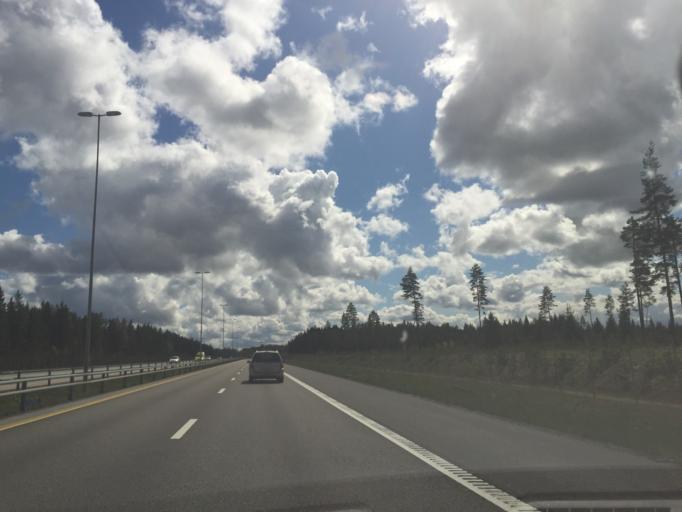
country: NO
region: Akershus
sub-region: Ullensaker
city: Jessheim
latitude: 60.2060
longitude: 11.1869
